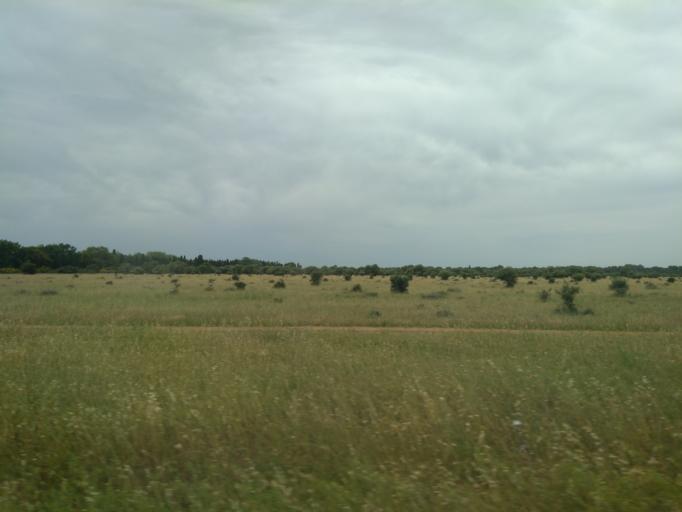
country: FR
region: Provence-Alpes-Cote d'Azur
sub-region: Departement des Bouches-du-Rhone
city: Miramas
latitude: 43.6211
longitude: 5.0154
